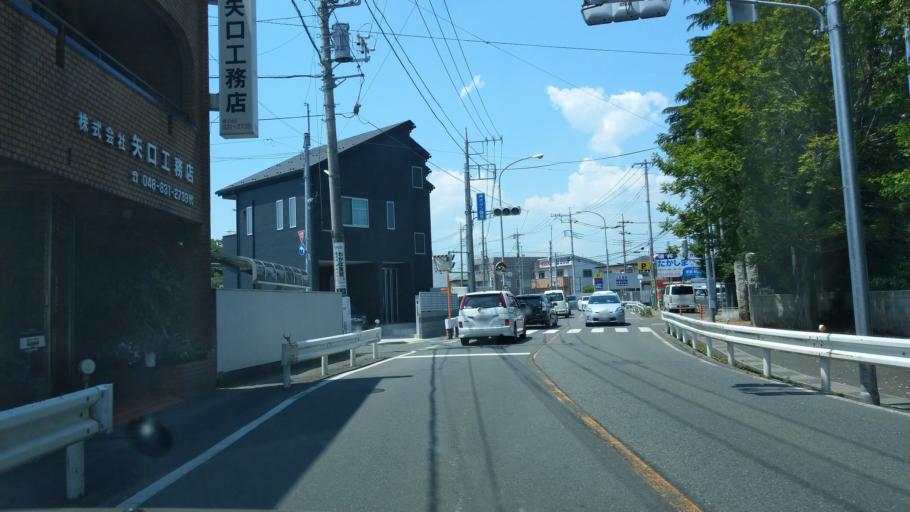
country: JP
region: Saitama
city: Yono
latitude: 35.8823
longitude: 139.6519
